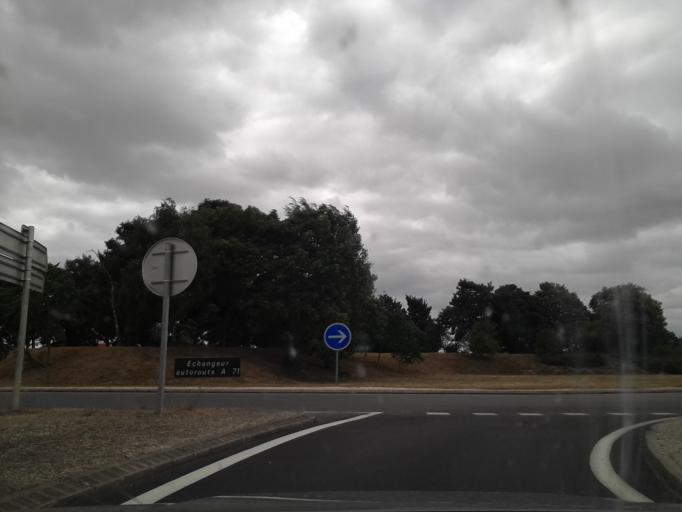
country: FR
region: Centre
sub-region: Departement du Cher
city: La Chapelle-Saint-Ursin
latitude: 47.0475
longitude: 2.3443
